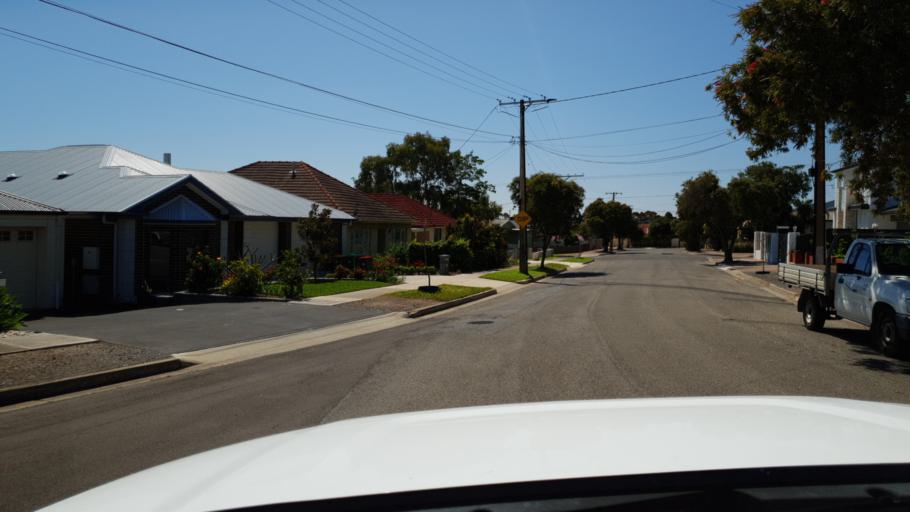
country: AU
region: South Australia
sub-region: Holdfast Bay
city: Seacliff Park
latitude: -35.0287
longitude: 138.5299
